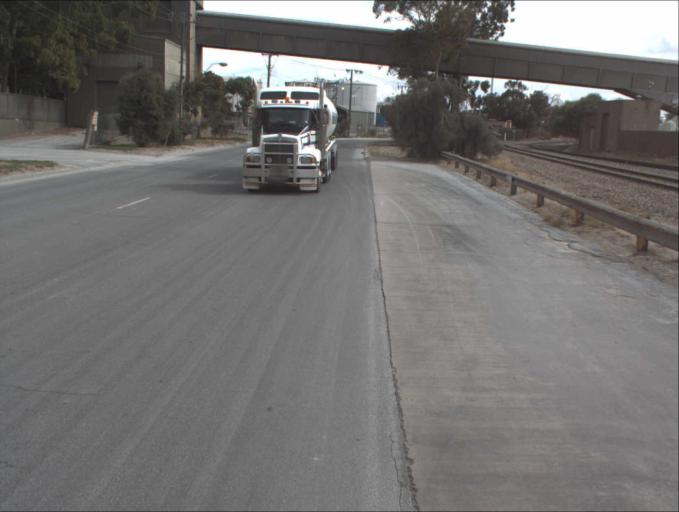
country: AU
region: South Australia
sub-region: Port Adelaide Enfield
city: Birkenhead
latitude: -34.8321
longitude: 138.5040
